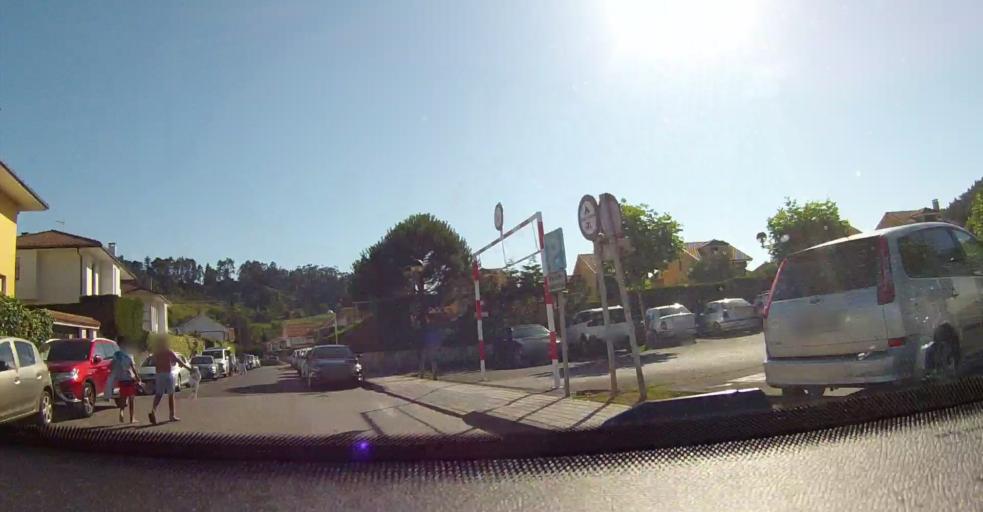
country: ES
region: Asturias
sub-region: Province of Asturias
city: Ribadesella
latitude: 43.4675
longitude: -5.0767
